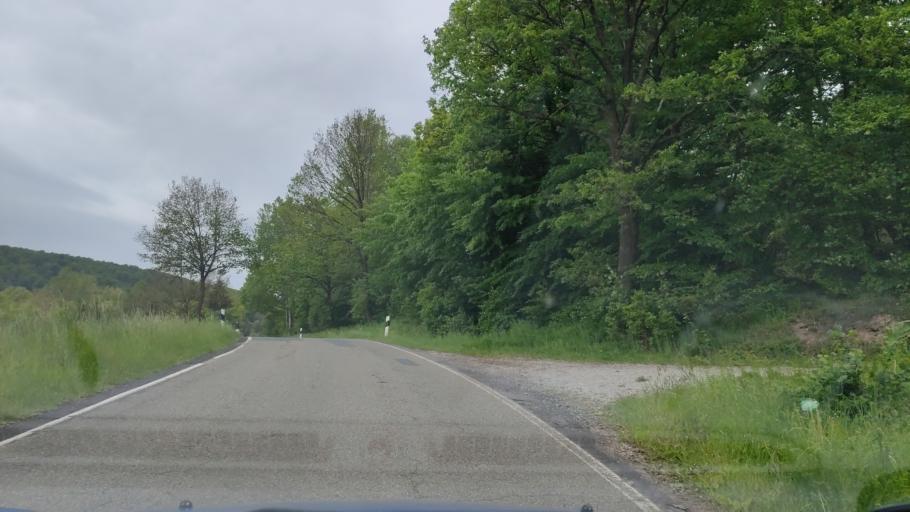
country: DE
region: Lower Saxony
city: Hardegsen
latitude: 51.7015
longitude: 9.7376
